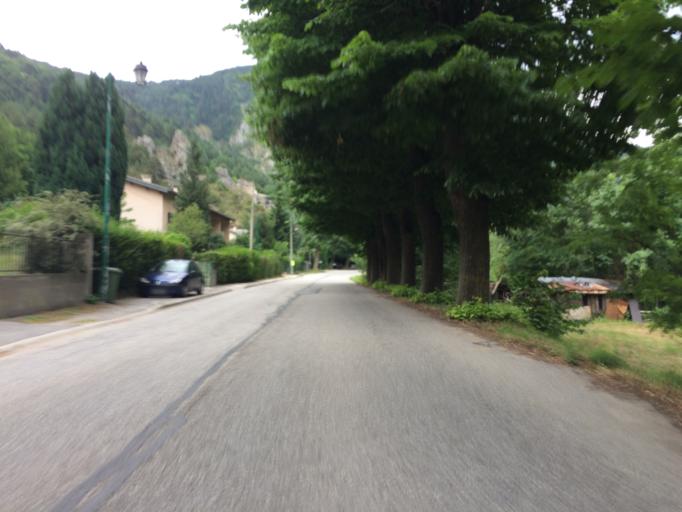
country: FR
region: Provence-Alpes-Cote d'Azur
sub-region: Departement des Alpes-Maritimes
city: Tende
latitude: 44.0799
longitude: 7.5981
